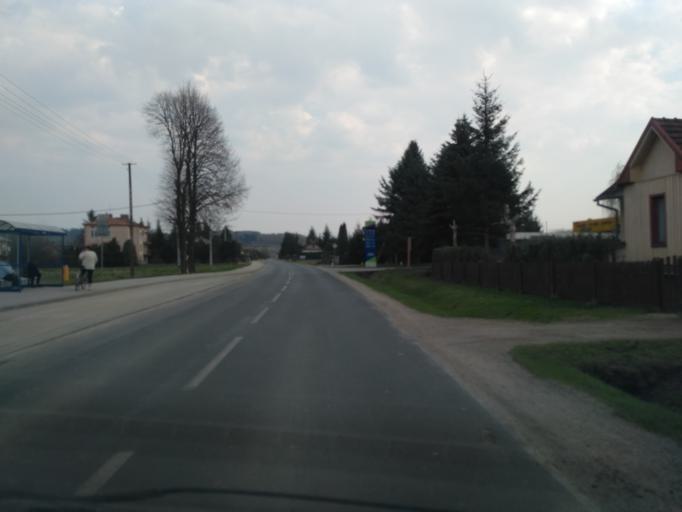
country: PL
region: Subcarpathian Voivodeship
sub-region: Powiat strzyzowski
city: Strzyzow
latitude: 49.8415
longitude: 21.8182
